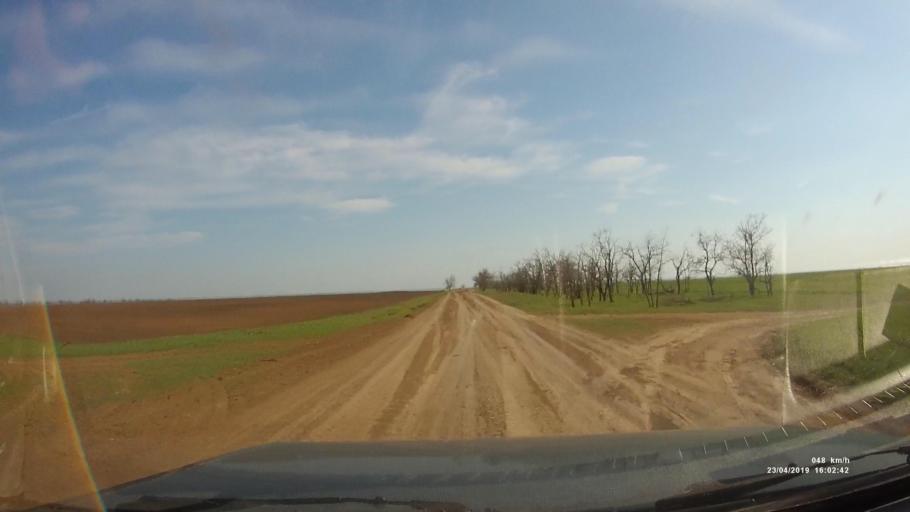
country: RU
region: Rostov
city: Remontnoye
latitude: 46.4923
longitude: 43.1071
